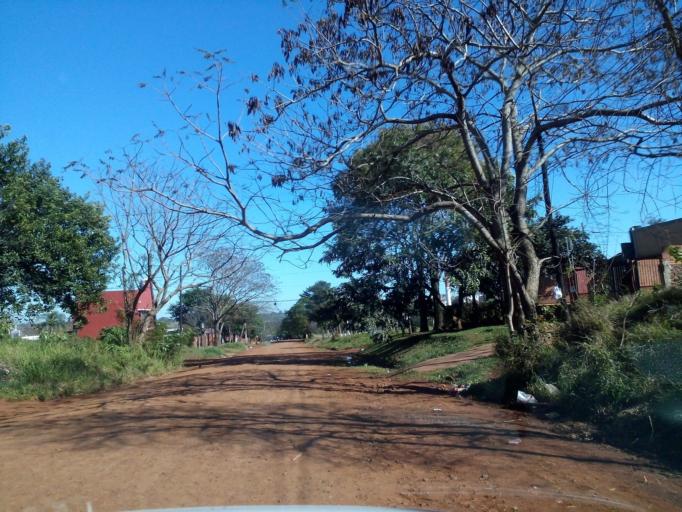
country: AR
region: Misiones
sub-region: Departamento de Capital
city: Posadas
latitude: -27.3761
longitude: -55.9457
